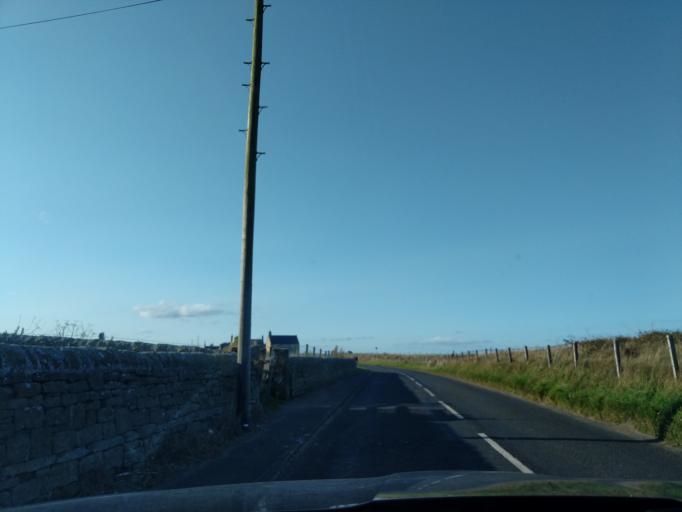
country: GB
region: England
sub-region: Northumberland
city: Lynemouth
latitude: 55.2324
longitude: -1.5339
